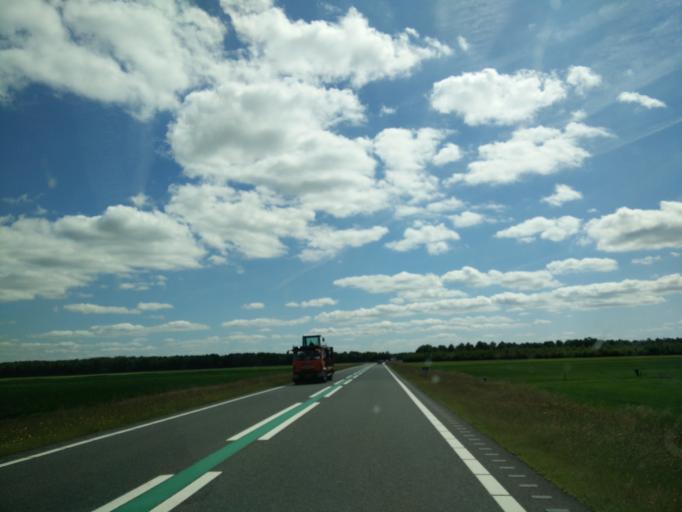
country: NL
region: Drenthe
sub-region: Gemeente Coevorden
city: Sleen
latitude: 52.7967
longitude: 6.8150
